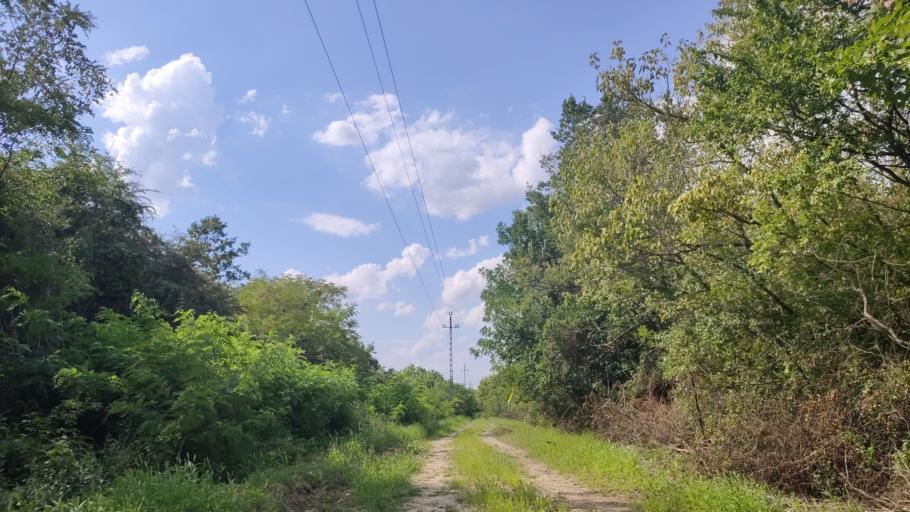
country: HU
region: Pest
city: Toeroekbalint
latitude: 47.4622
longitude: 18.8726
